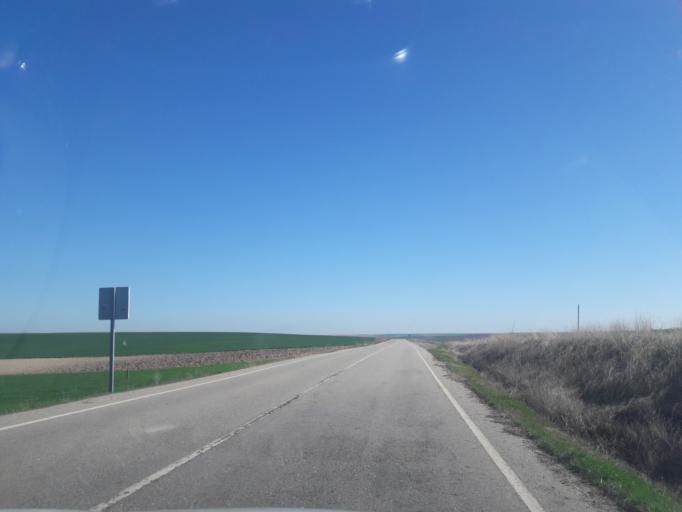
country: ES
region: Castille and Leon
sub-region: Provincia de Salamanca
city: Salmoral
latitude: 40.8178
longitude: -5.2117
